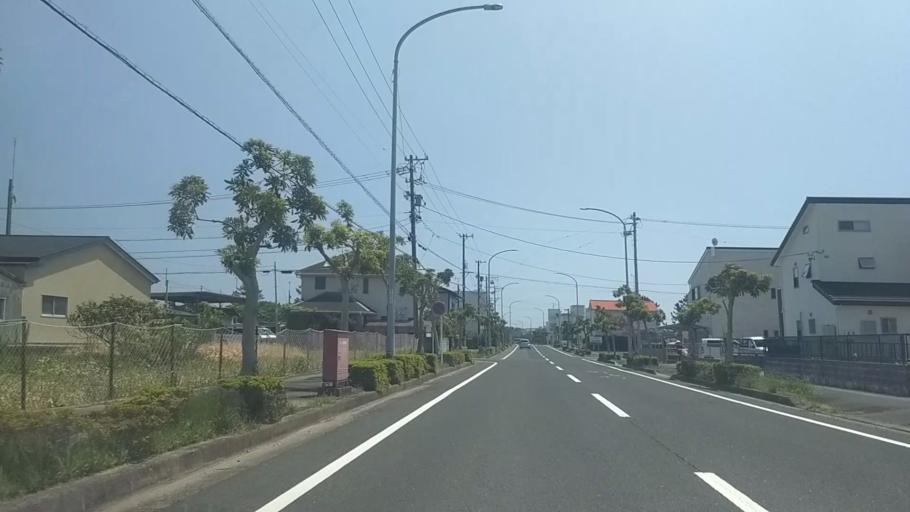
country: JP
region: Shizuoka
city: Kosai-shi
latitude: 34.6878
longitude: 137.5696
